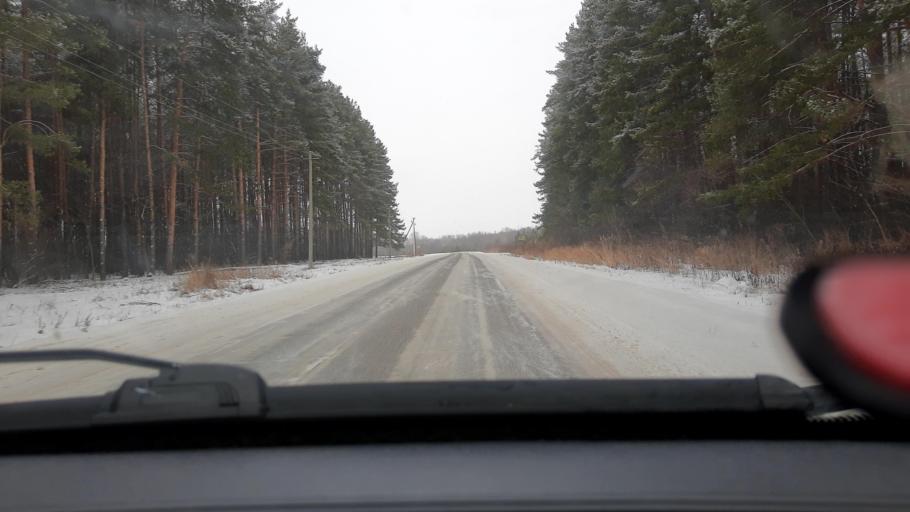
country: RU
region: Bashkortostan
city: Iglino
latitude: 54.6774
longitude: 56.4183
